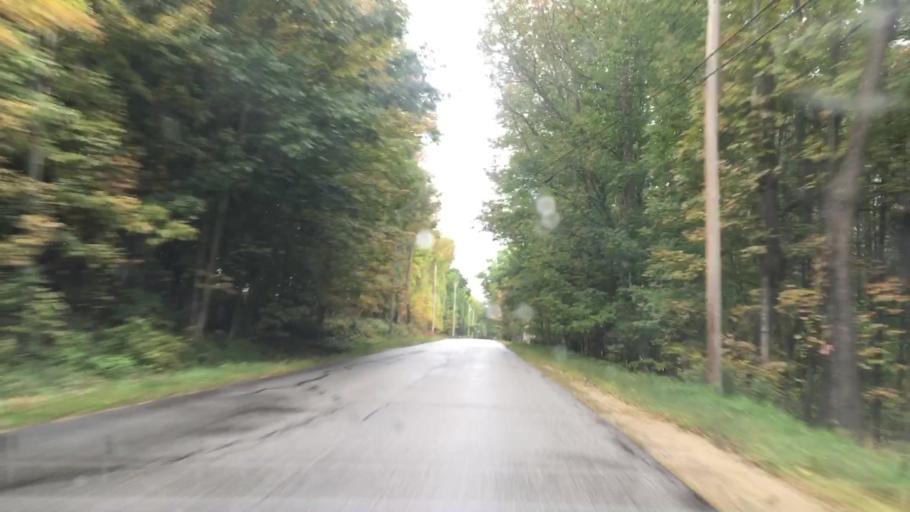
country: US
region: Maine
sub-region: Cumberland County
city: Harrison
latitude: 44.0623
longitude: -70.6260
